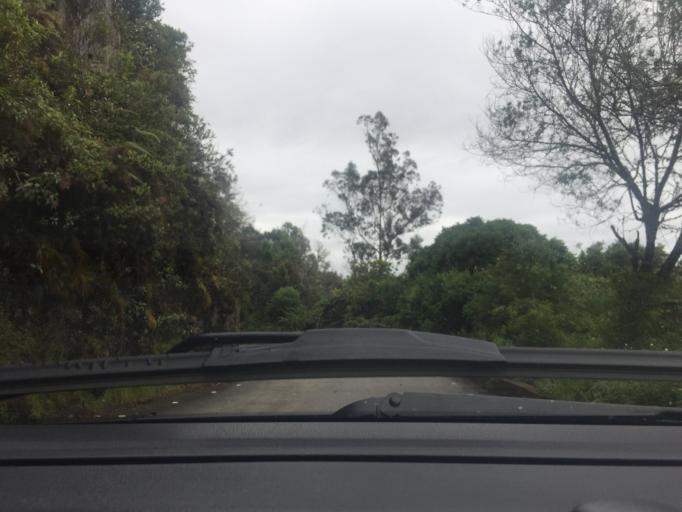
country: CO
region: Cundinamarca
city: Junin
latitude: 4.8232
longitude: -73.7529
